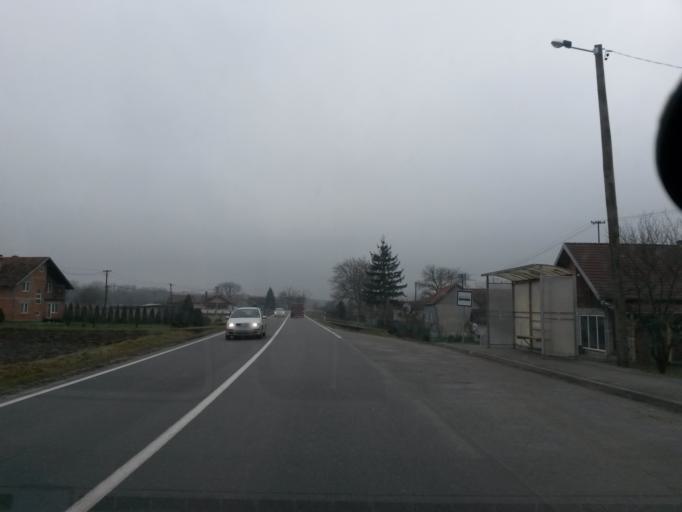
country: HR
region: Vukovarsko-Srijemska
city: Bosnjaci
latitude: 45.0019
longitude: 18.7811
